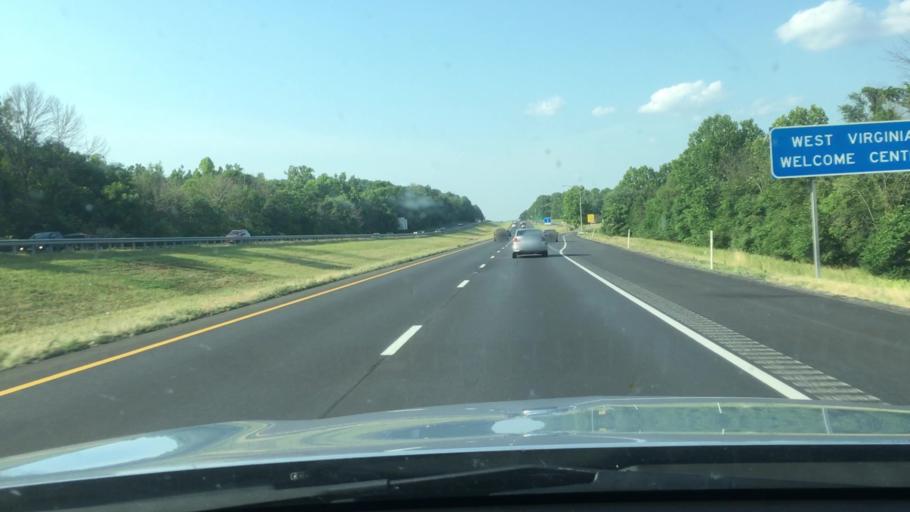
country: US
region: West Virginia
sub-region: Berkeley County
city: Inwood
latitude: 39.3167
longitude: -78.0743
